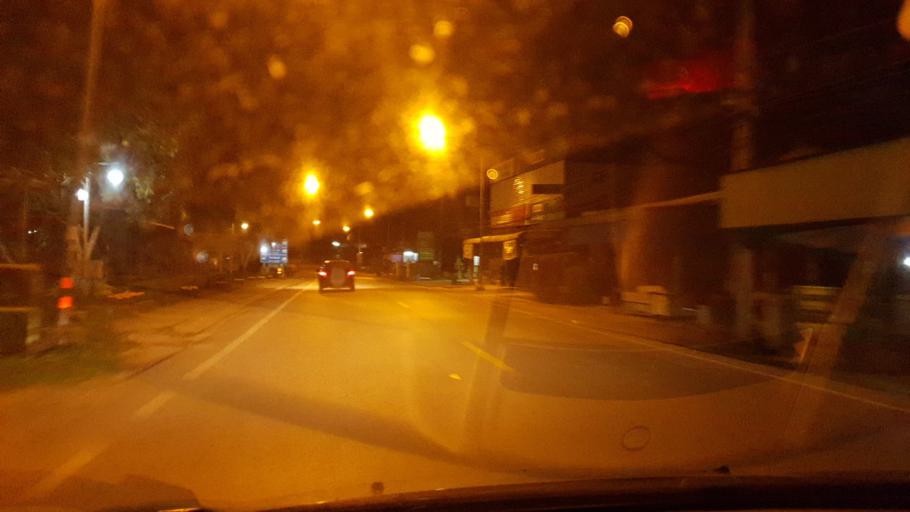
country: TH
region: Mae Hong Son
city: Khun Yuam
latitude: 18.8313
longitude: 97.9351
